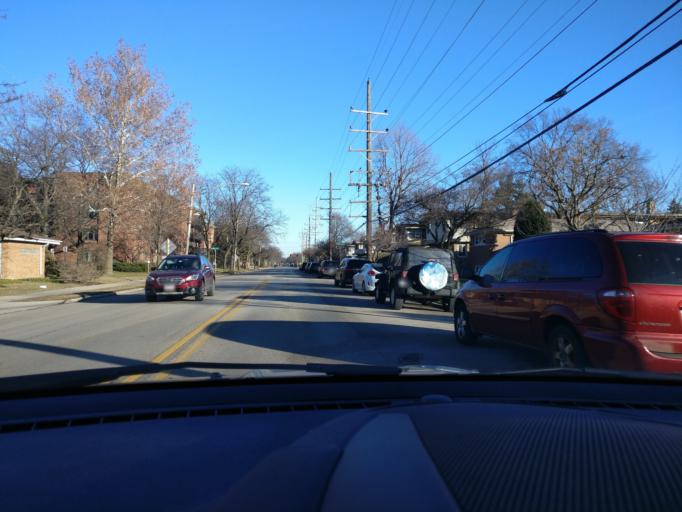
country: US
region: Illinois
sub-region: Cook County
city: Skokie
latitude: 42.0481
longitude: -87.7175
